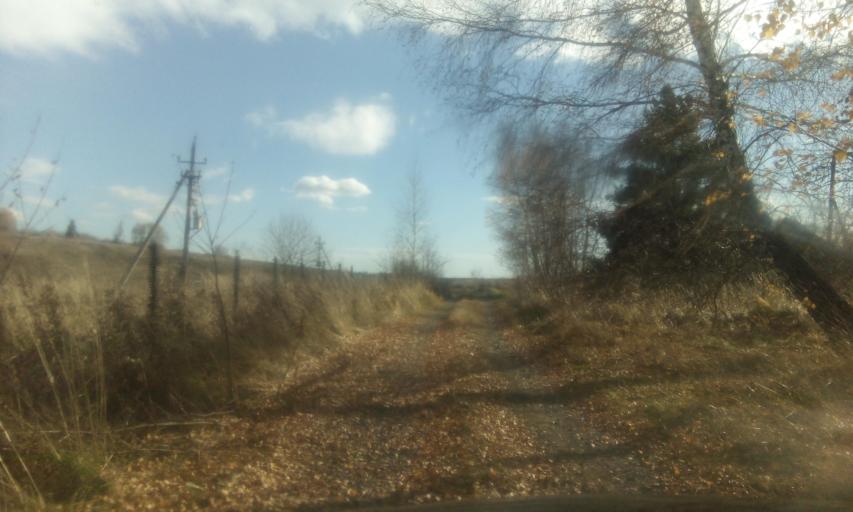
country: RU
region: Tula
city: Dubovka
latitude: 53.9156
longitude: 38.0676
